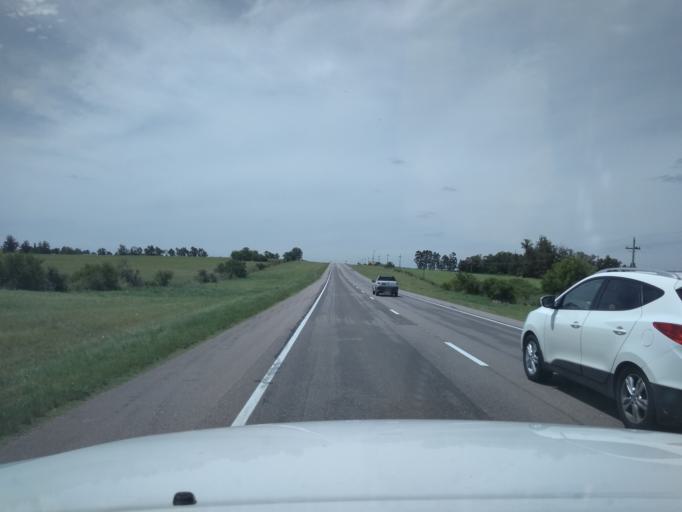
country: UY
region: Florida
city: Florida
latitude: -34.2176
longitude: -56.2079
